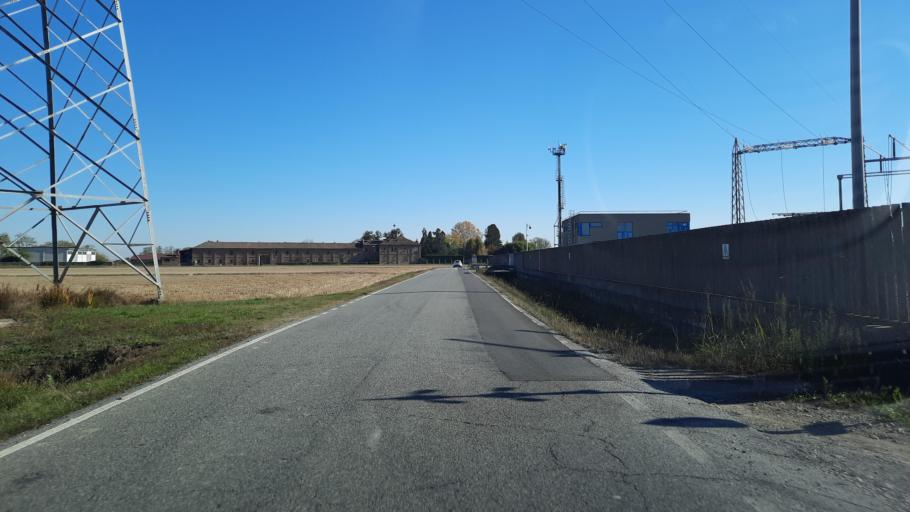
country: IT
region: Piedmont
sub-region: Provincia di Alessandria
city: Balzola
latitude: 45.1861
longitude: 8.4288
